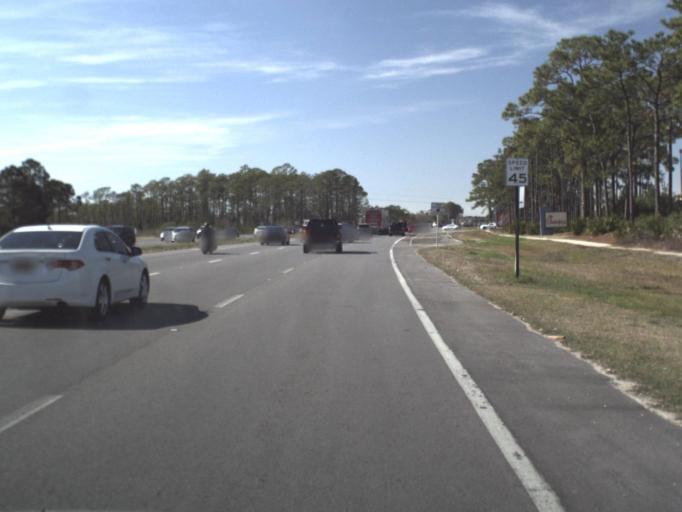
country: US
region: Florida
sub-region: Bay County
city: Panama City Beach
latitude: 30.1966
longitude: -85.8127
